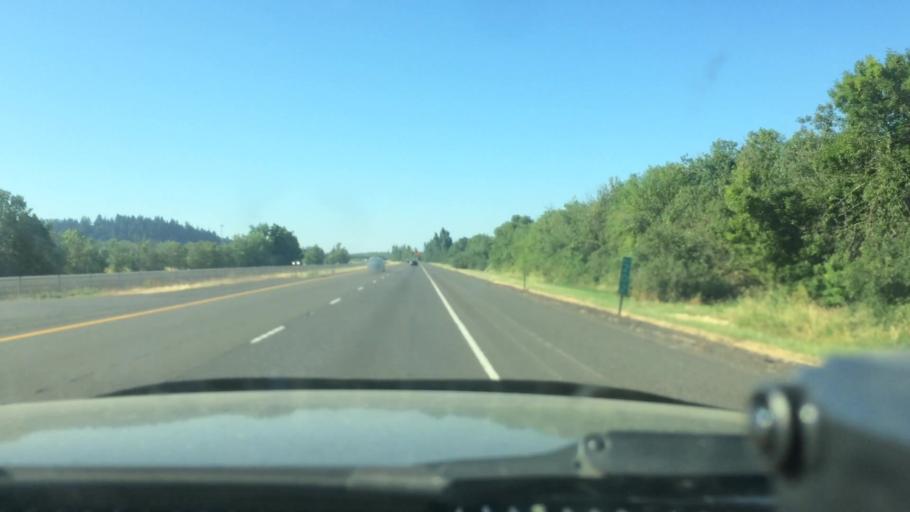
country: US
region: Oregon
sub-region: Lane County
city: Coburg
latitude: 44.1791
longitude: -123.0608
